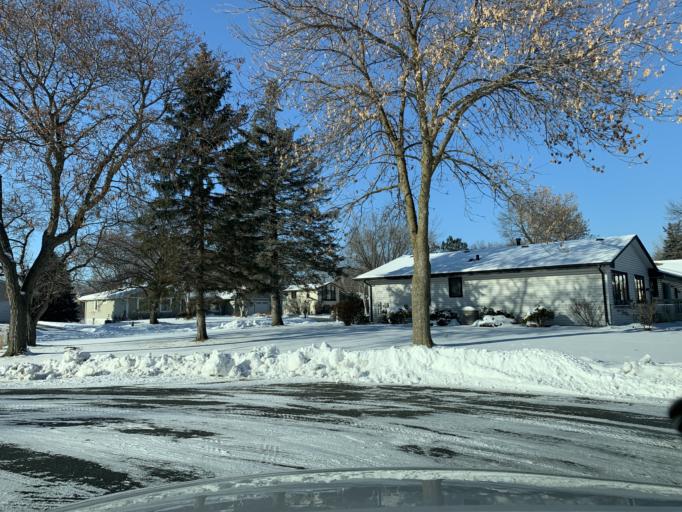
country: US
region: Minnesota
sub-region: Scott County
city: Savage
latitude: 44.8313
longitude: -93.3543
